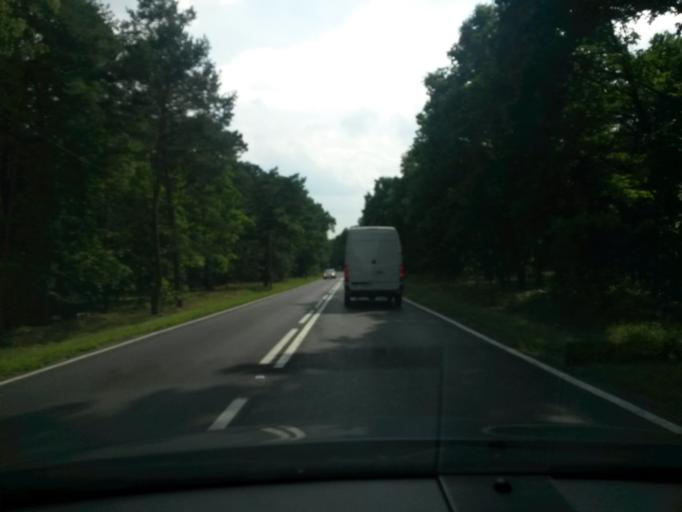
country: PL
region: Greater Poland Voivodeship
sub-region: Powiat poznanski
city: Kornik
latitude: 52.1731
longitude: 17.0440
